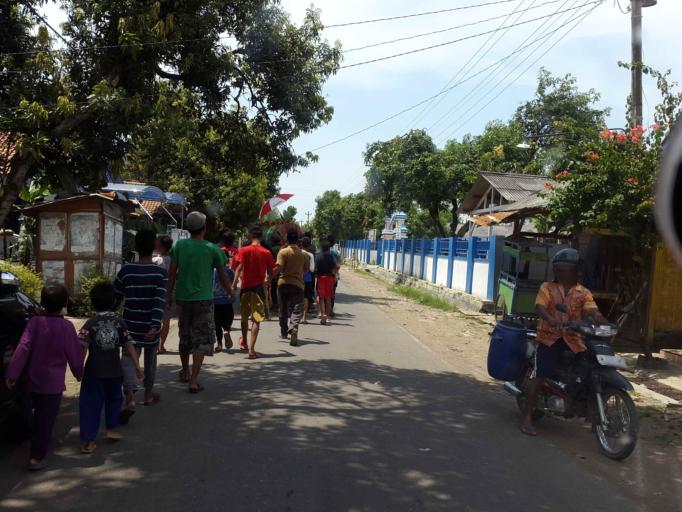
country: ID
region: Central Java
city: Petarukan
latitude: -6.8640
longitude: 109.4207
